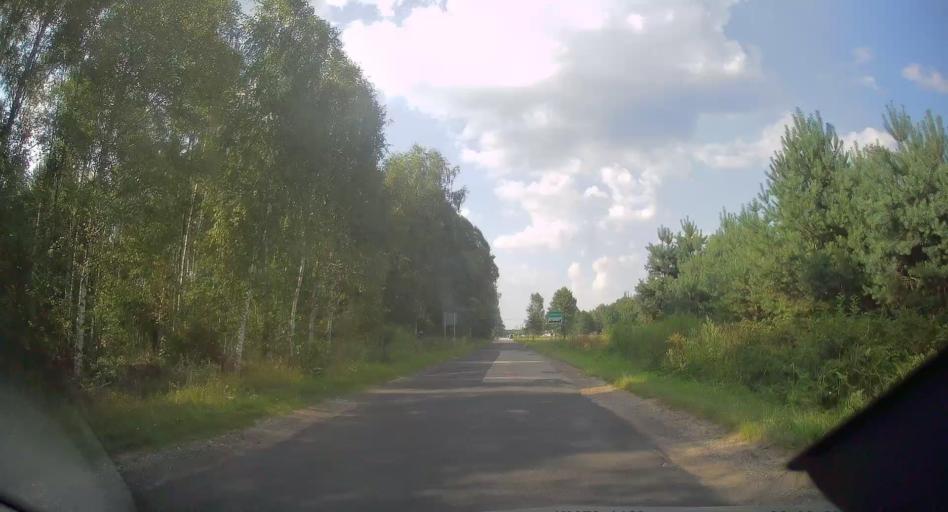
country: PL
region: Swietokrzyskie
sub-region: Powiat konecki
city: Radoszyce
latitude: 51.1098
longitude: 20.2639
